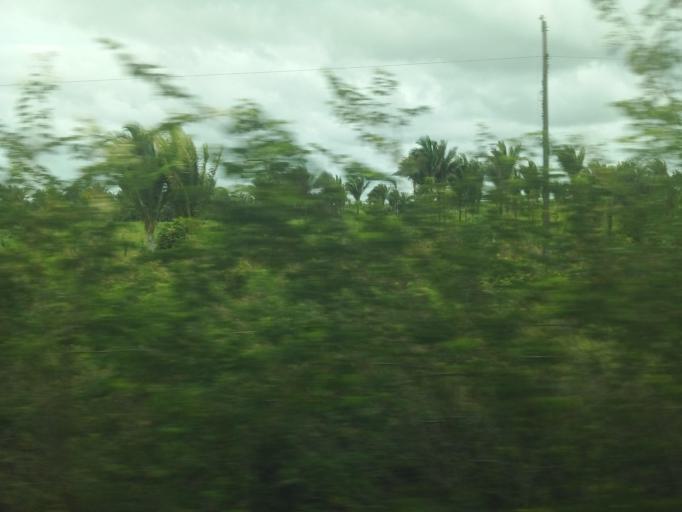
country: BR
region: Maranhao
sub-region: Itapecuru Mirim
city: Itapecuru Mirim
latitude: -3.2127
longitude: -44.3992
